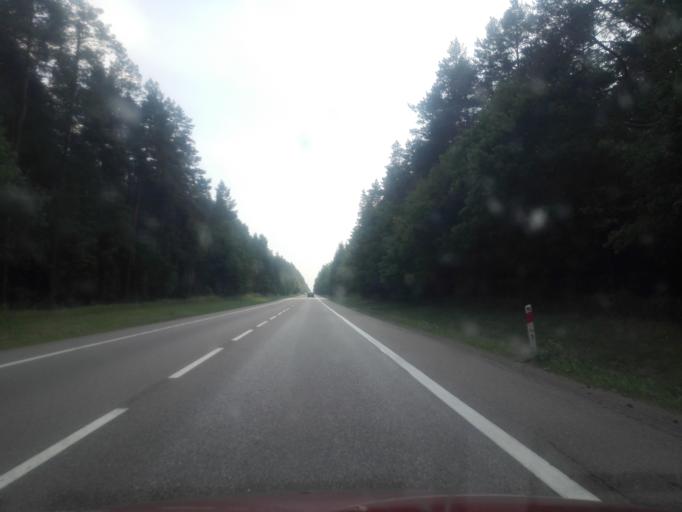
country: PL
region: Podlasie
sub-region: Suwalki
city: Suwalki
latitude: 54.0504
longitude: 22.9373
